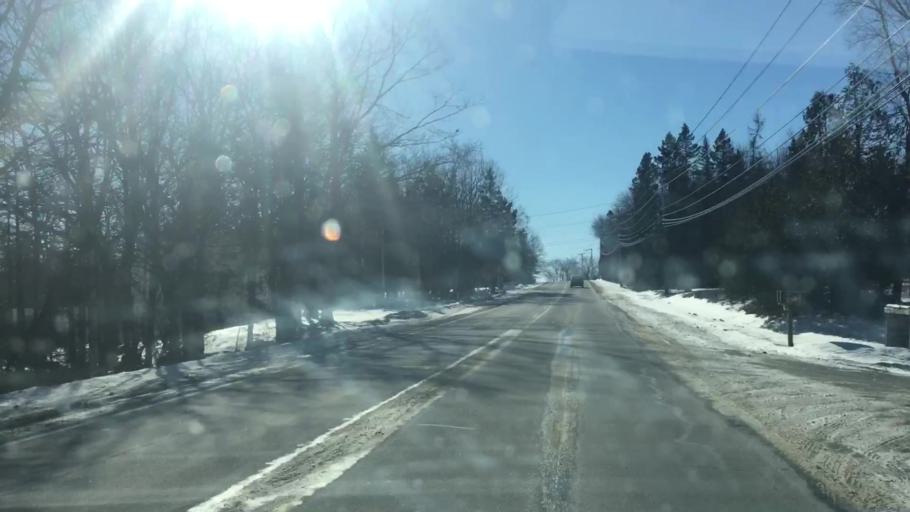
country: US
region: Maine
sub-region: Hancock County
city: Ellsworth
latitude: 44.5119
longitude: -68.4367
